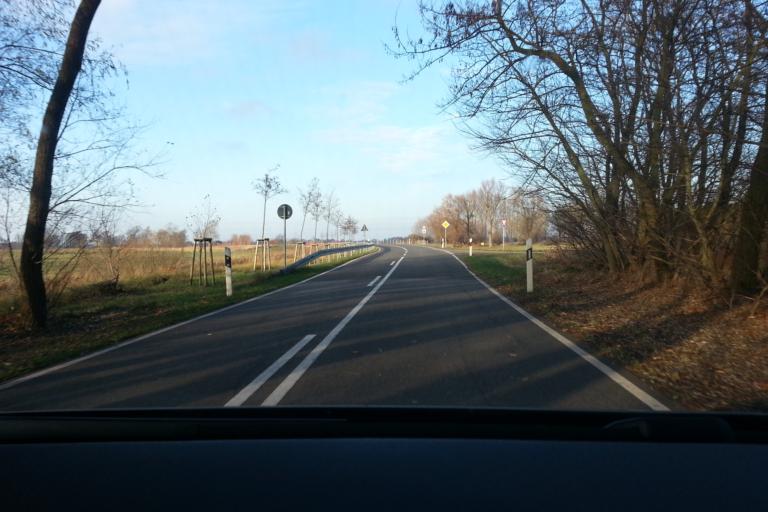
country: DE
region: Mecklenburg-Vorpommern
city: Strasburg
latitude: 53.6219
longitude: 13.7661
